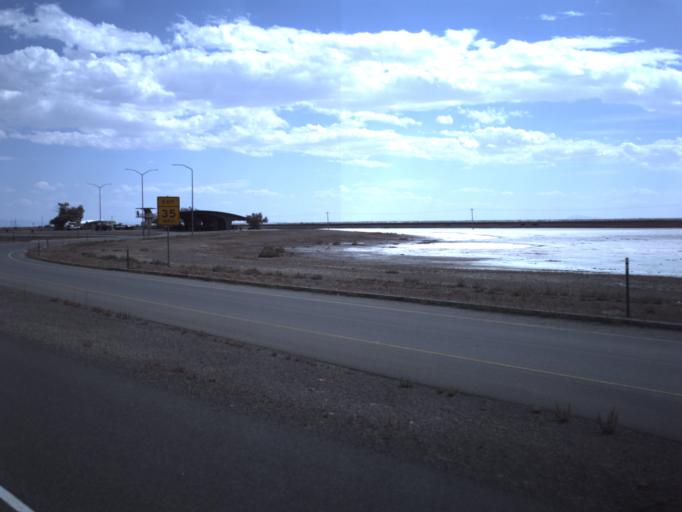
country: US
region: Utah
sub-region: Tooele County
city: Wendover
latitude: 40.7386
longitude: -113.8600
